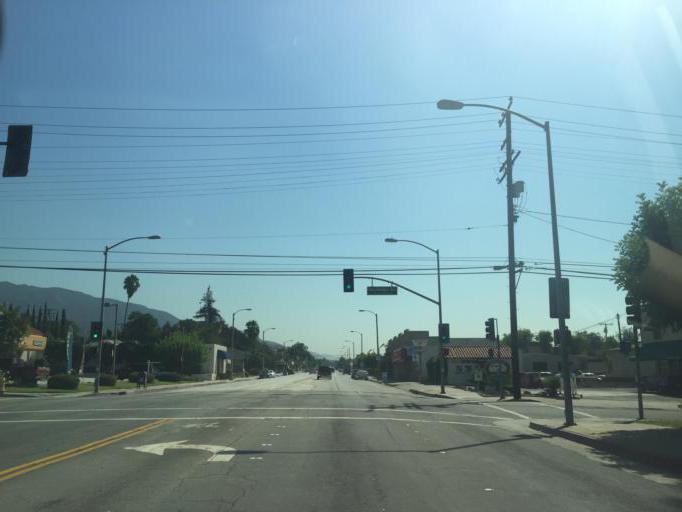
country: US
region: California
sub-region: Los Angeles County
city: Monrovia
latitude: 34.1512
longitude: -118.0101
